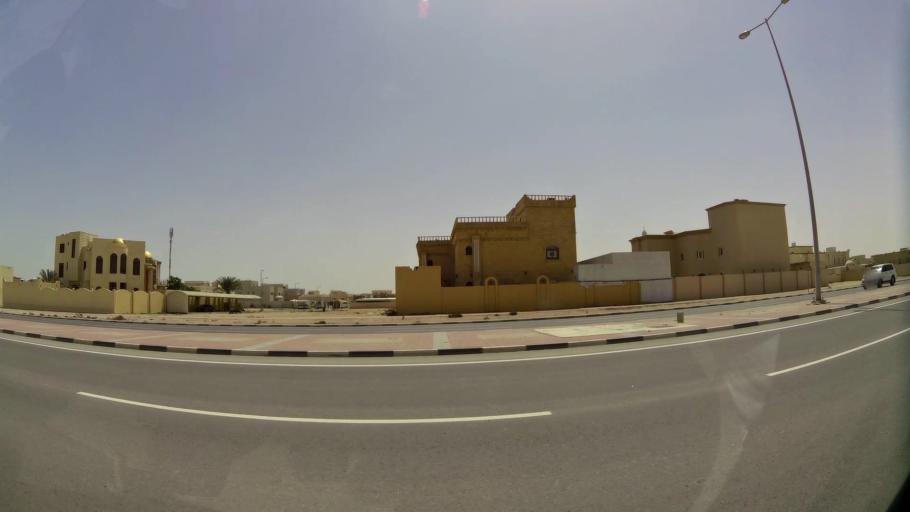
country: QA
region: Baladiyat Umm Salal
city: Umm Salal Muhammad
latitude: 25.4079
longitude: 51.4434
